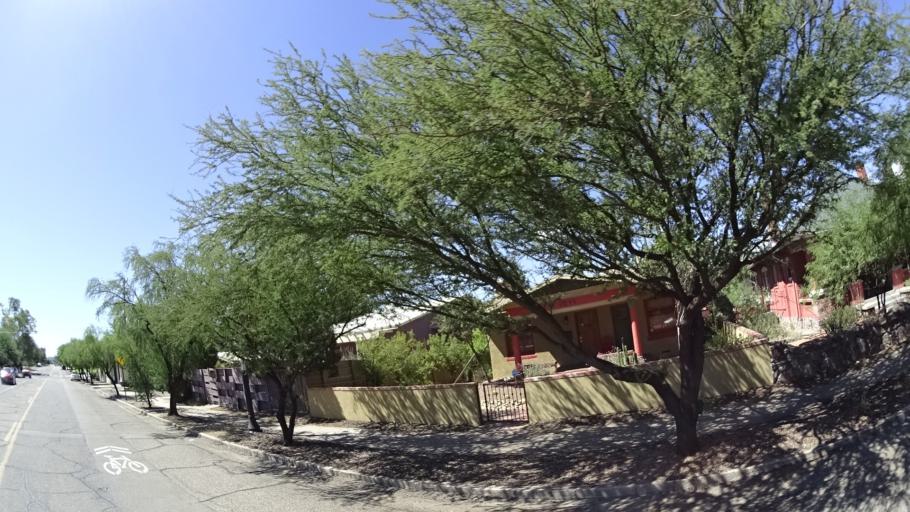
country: US
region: Arizona
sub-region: Pima County
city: South Tucson
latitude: 32.2352
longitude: -110.9657
